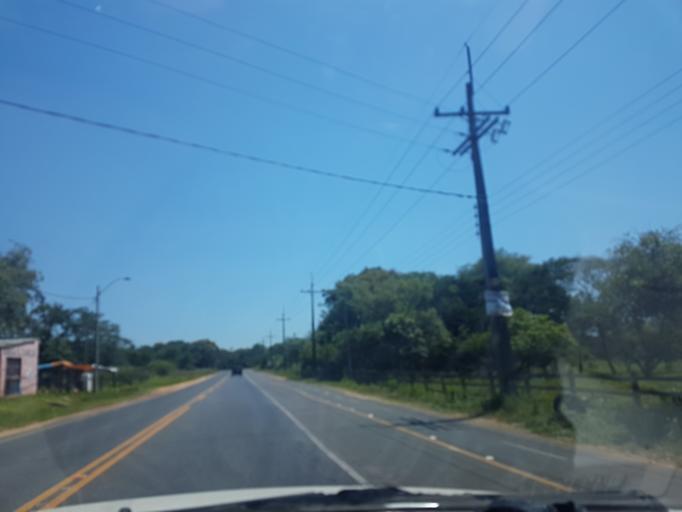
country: PY
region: Central
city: Aregua
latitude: -25.2321
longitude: -57.4194
